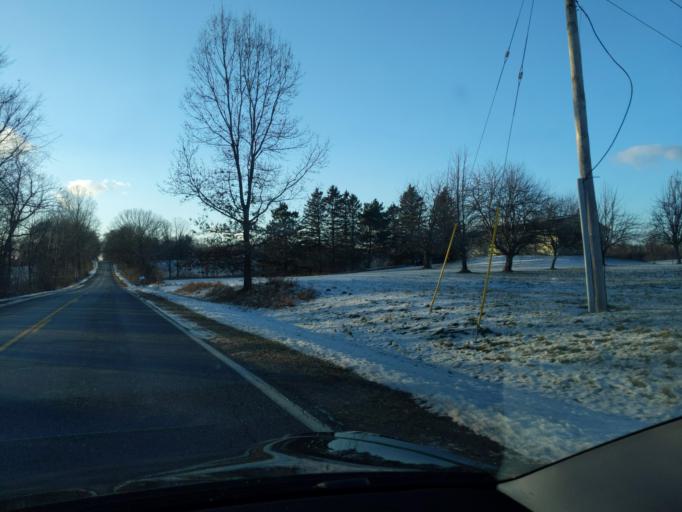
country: US
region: Michigan
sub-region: Ingham County
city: Stockbridge
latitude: 42.4462
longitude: -84.0884
